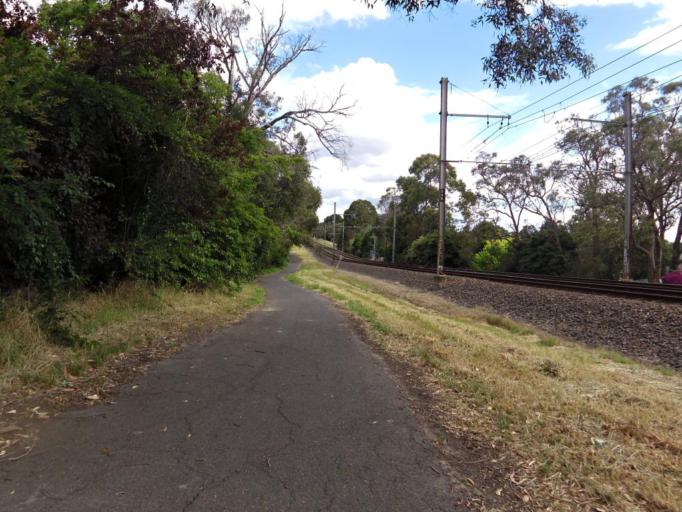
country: AU
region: Victoria
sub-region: Maroondah
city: Ringwood East
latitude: -37.8216
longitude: 145.2410
